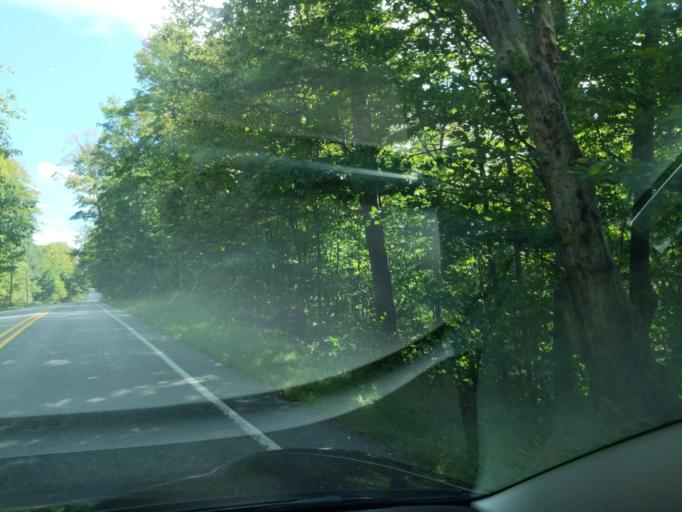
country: US
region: Michigan
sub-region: Antrim County
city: Bellaire
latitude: 44.9981
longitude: -85.2903
